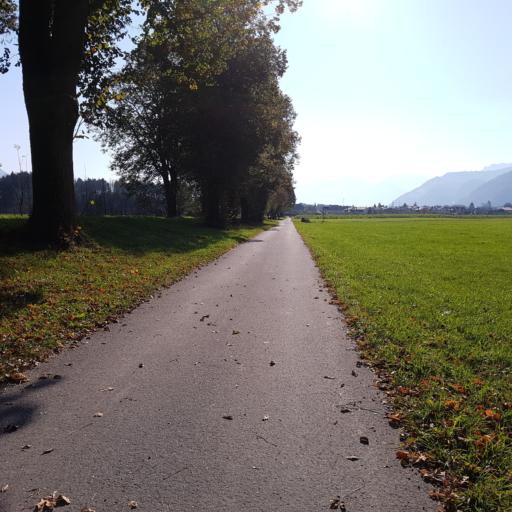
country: AT
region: Salzburg
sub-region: Politischer Bezirk Hallein
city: Puch bei Hallein
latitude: 47.7171
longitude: 13.0721
